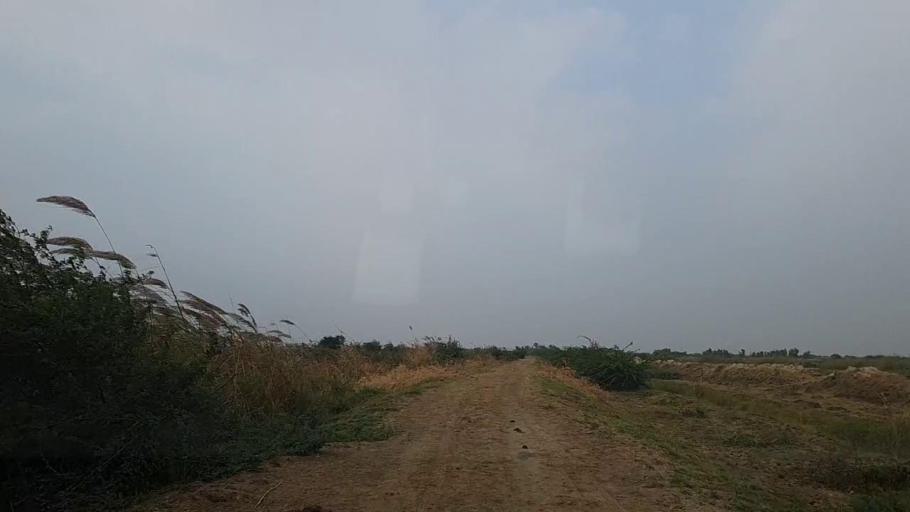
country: PK
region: Sindh
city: Mirpur Sakro
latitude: 24.6224
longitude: 67.5022
